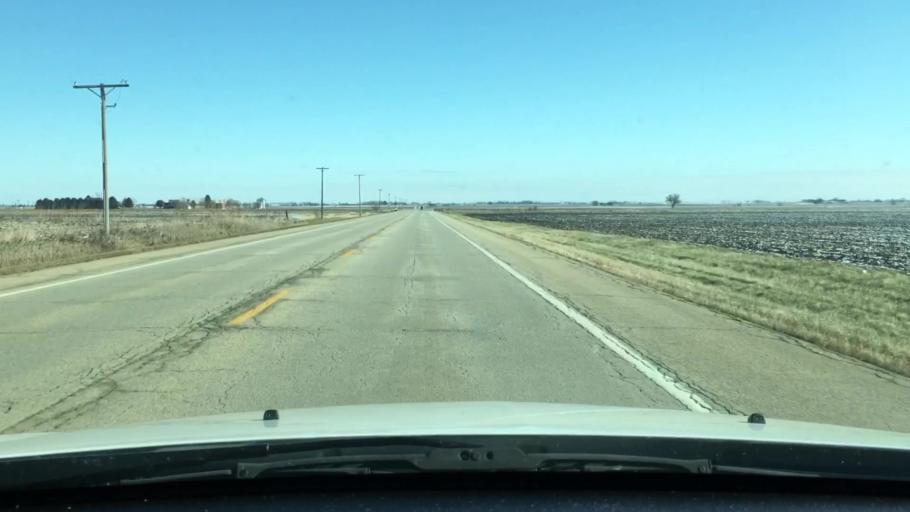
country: US
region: Illinois
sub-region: Ogle County
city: Hillcrest
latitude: 42.0074
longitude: -88.9919
